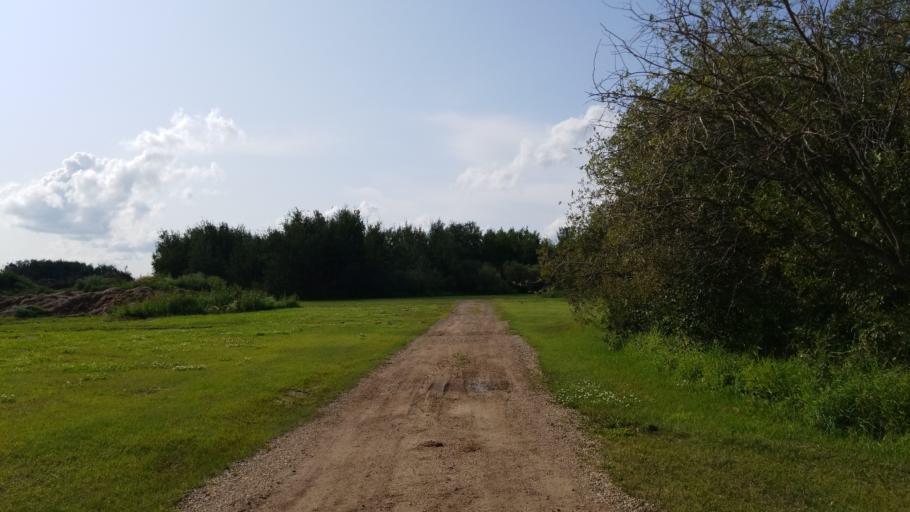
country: CA
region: Saskatchewan
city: Lloydminster
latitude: 53.2565
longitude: -110.0459
